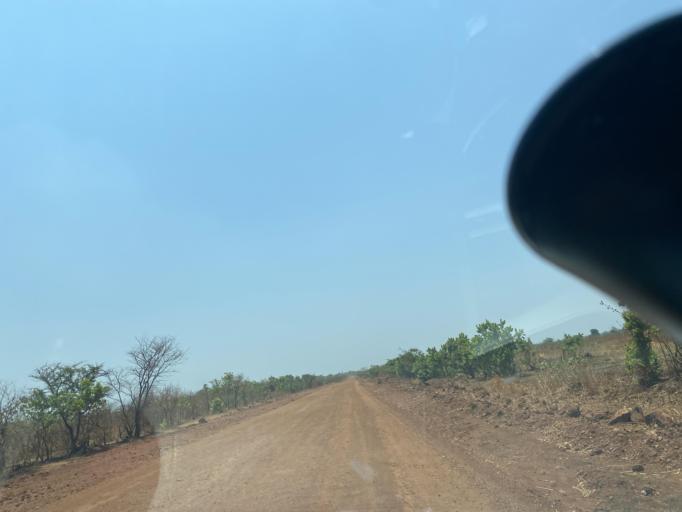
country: ZM
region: Lusaka
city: Lusaka
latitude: -15.4568
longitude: 27.9376
